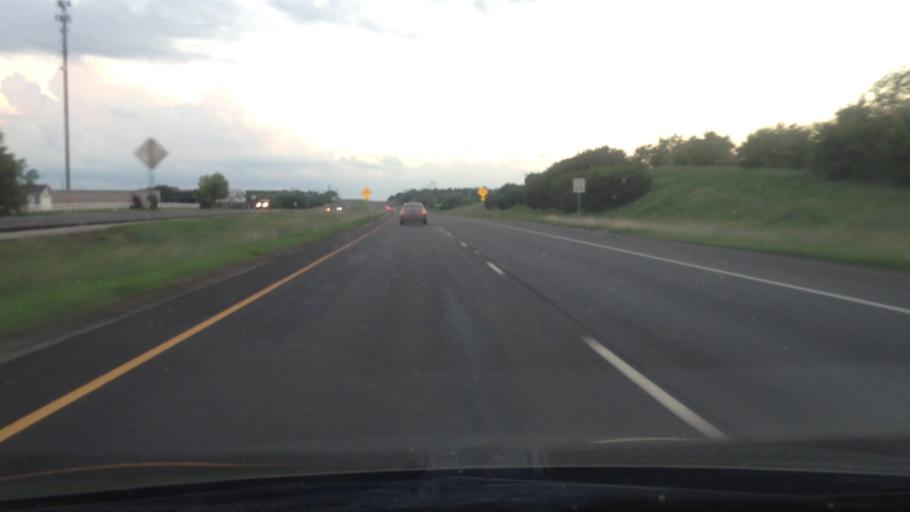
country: US
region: Texas
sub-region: Hood County
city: DeCordova
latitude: 32.5243
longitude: -97.6247
